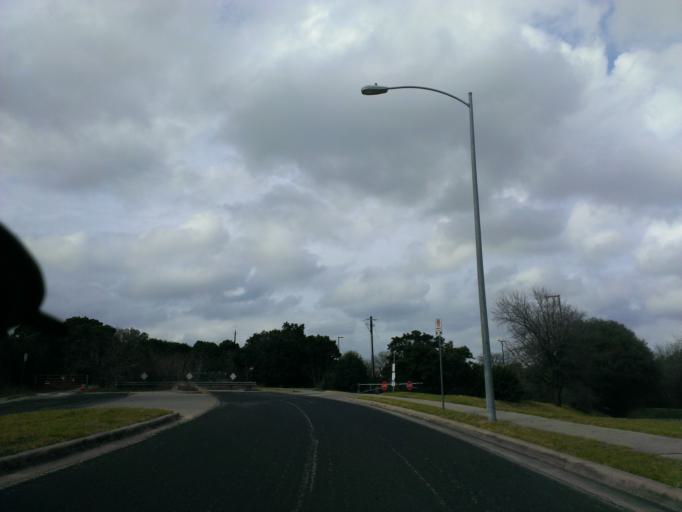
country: US
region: Texas
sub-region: Travis County
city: Wells Branch
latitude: 30.3941
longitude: -97.6766
